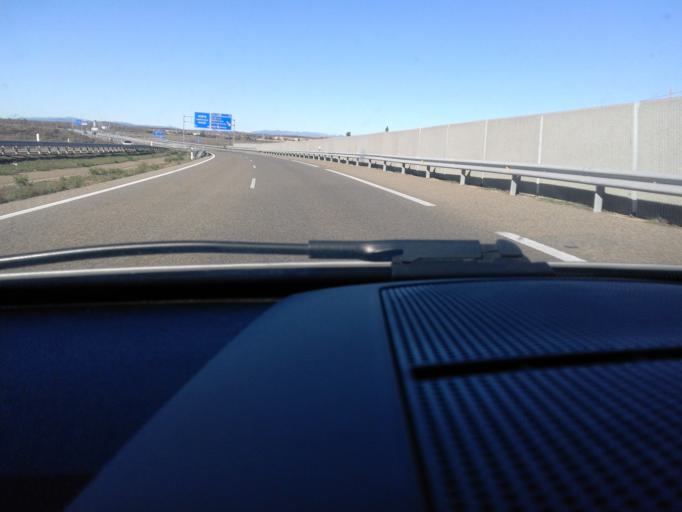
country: ES
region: Castille and Leon
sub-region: Provincia de Leon
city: Valverde de la Virgen
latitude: 42.5599
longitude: -5.6379
